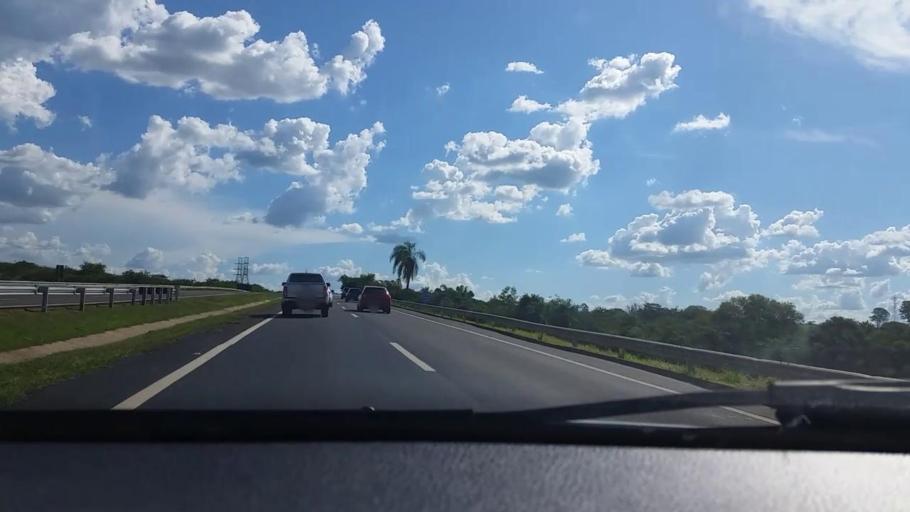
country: BR
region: Sao Paulo
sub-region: Bauru
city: Bauru
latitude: -22.4081
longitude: -49.0992
